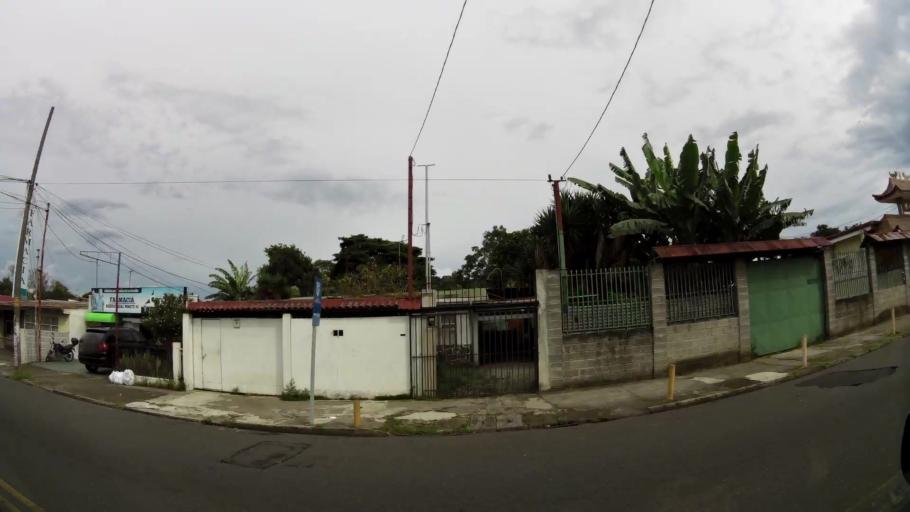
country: CR
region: San Jose
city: Calle Blancos
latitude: 9.9620
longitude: -84.0670
